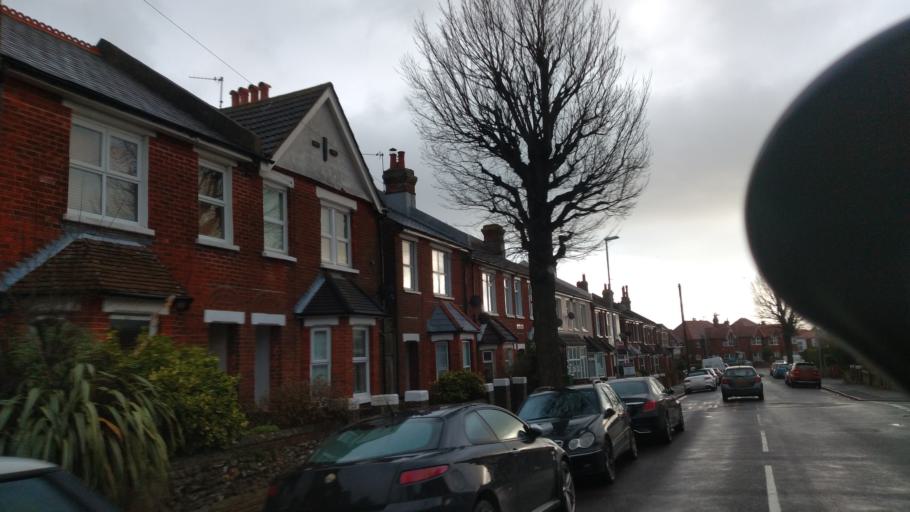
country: GB
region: England
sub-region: East Sussex
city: Eastbourne
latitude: 50.7766
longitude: 0.2577
